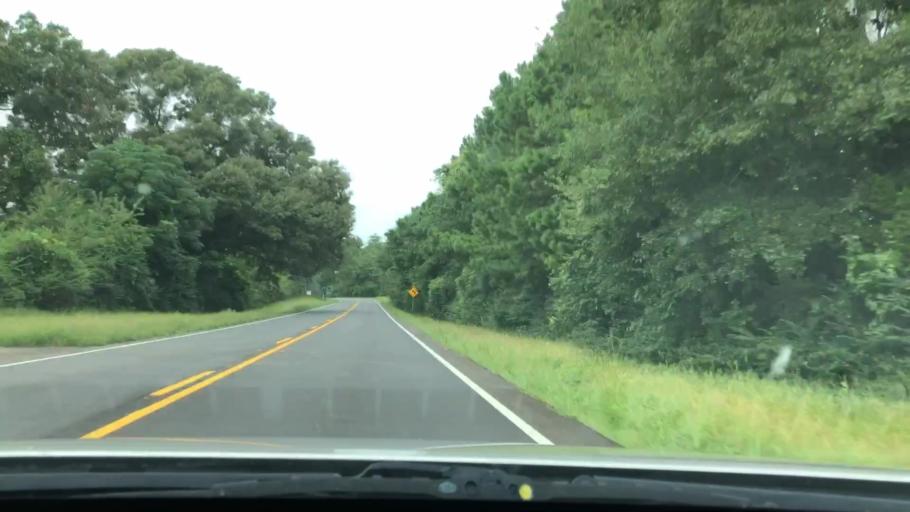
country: US
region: Georgia
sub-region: Upson County
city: Hannahs Mill
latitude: 33.0130
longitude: -84.4750
